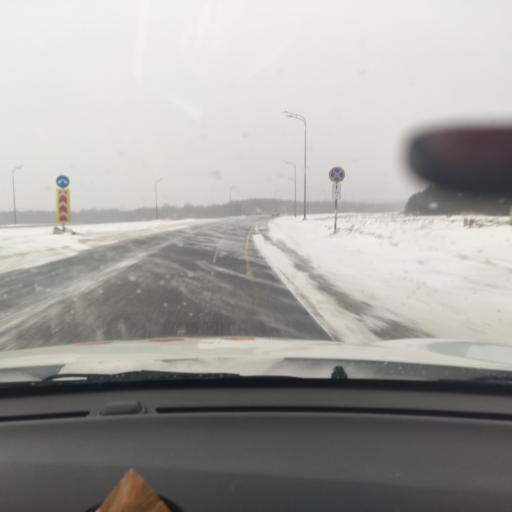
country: RU
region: Tatarstan
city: Verkhniy Uslon
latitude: 55.7063
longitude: 48.8905
